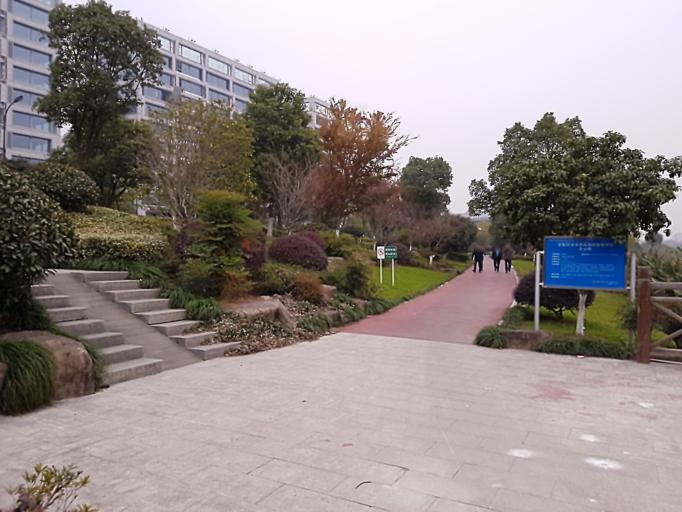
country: CN
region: Zhejiang Sheng
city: Cangqian
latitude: 30.2853
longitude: 120.0100
